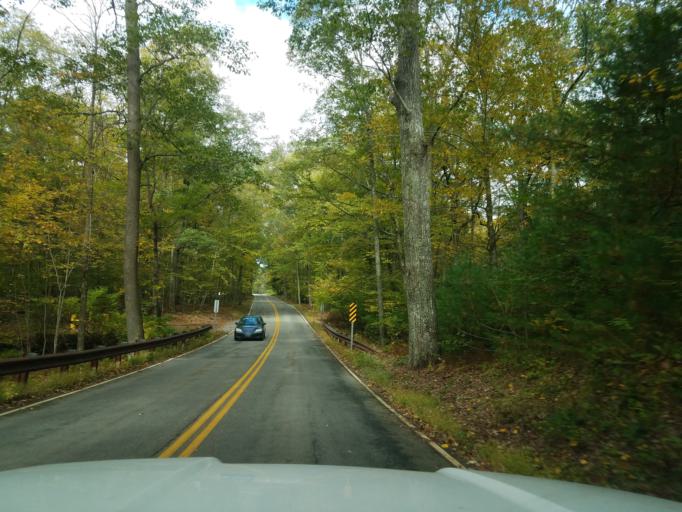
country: US
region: Connecticut
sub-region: Hartford County
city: Manchester
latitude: 41.7780
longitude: -72.4727
